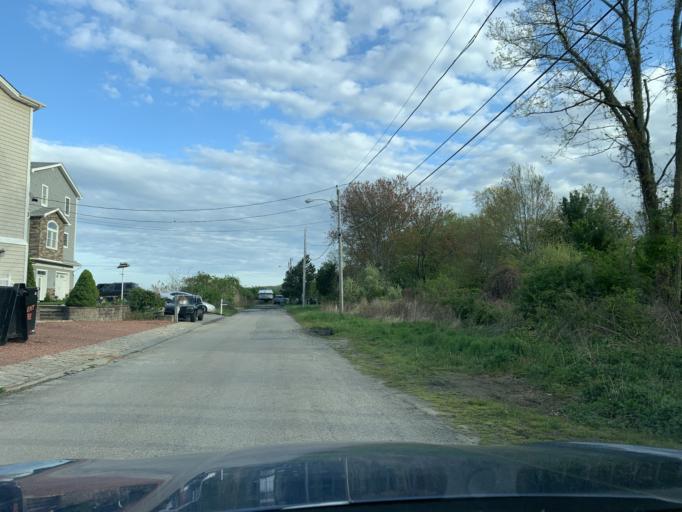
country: US
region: Rhode Island
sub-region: Kent County
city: Warwick
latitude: 41.6604
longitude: -71.4112
